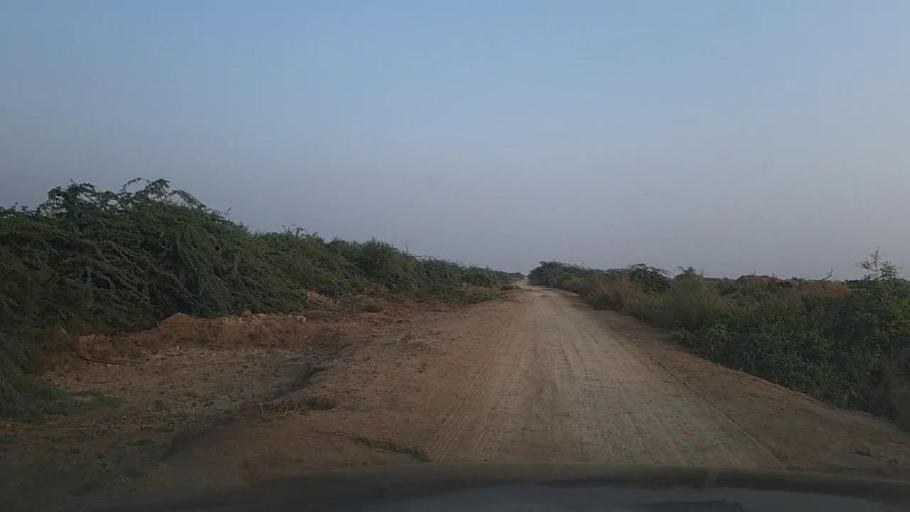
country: PK
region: Sindh
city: Mirpur Batoro
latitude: 24.5460
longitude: 68.3895
